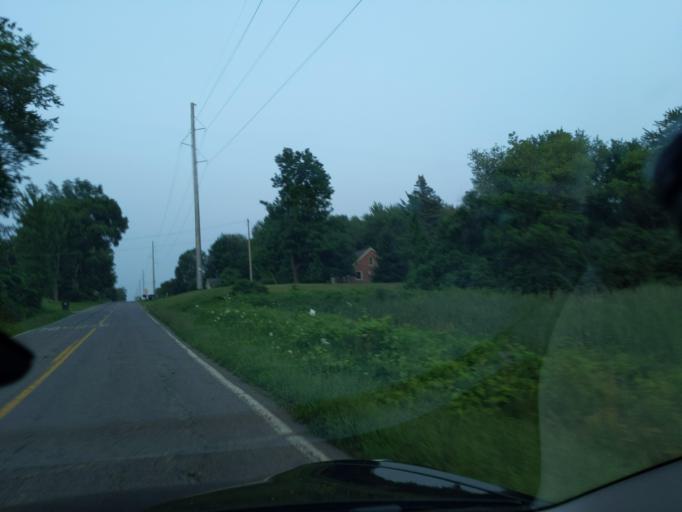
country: US
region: Michigan
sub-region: Jackson County
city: Jackson
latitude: 42.3275
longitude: -84.4609
